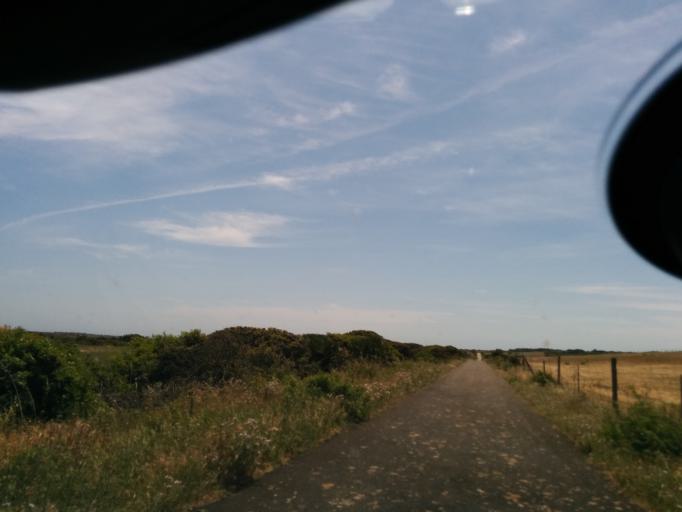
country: IT
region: Sardinia
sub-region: Provincia di Carbonia-Iglesias
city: Calasetta
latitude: 39.0459
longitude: 8.3856
